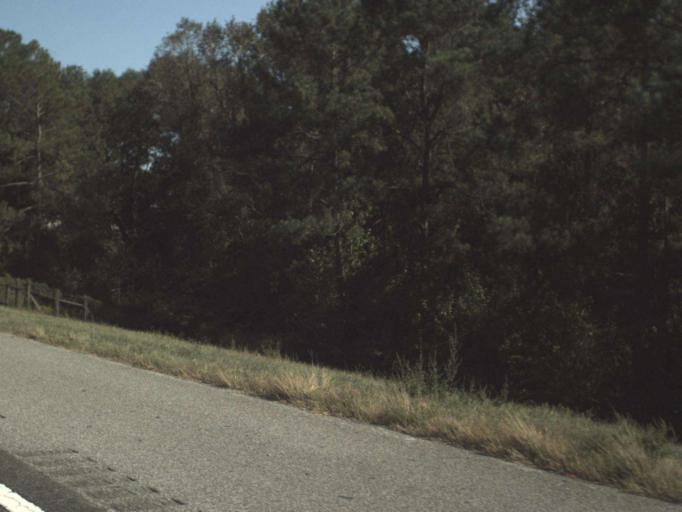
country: US
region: Florida
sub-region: Washington County
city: Chipley
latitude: 30.7465
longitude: -85.5428
